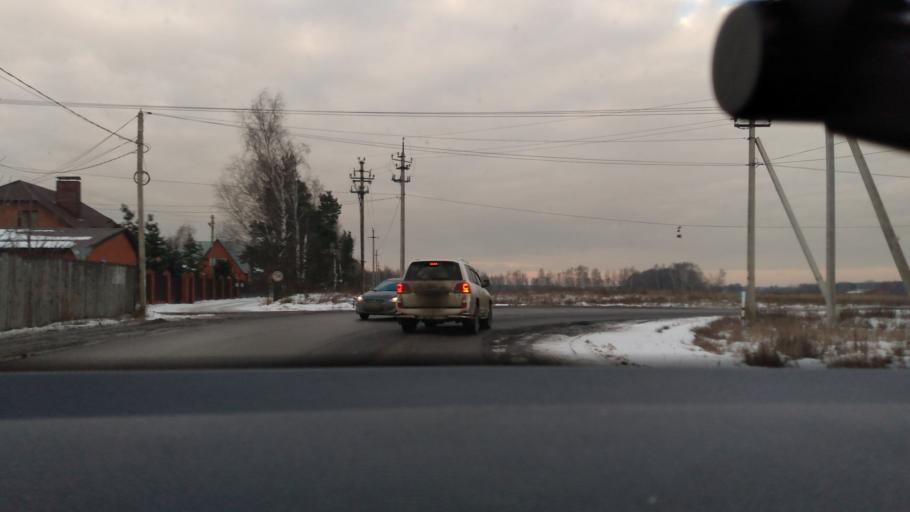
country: RU
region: Moskovskaya
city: Rodniki
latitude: 55.6813
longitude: 38.0969
